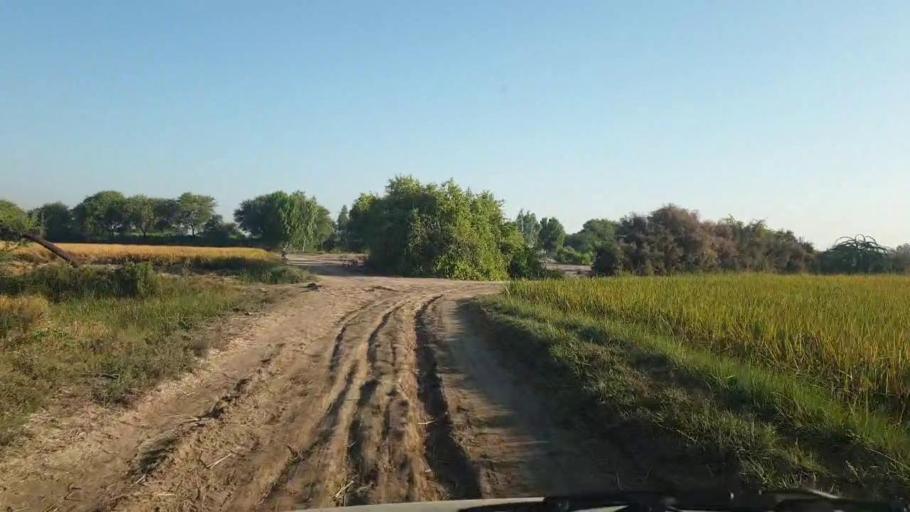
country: PK
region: Sindh
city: Talhar
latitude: 24.8024
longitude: 68.8192
